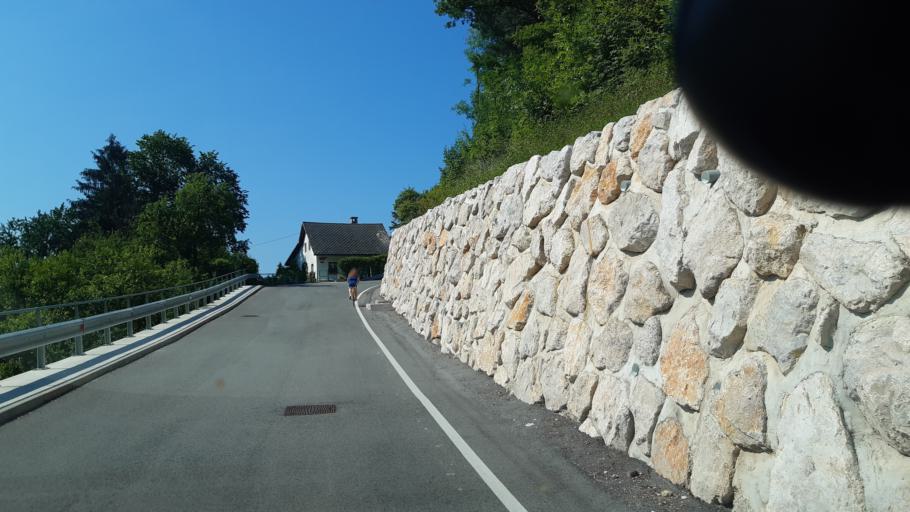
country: SI
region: Trzic
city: Bistrica pri Trzicu
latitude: 46.3566
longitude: 14.2892
